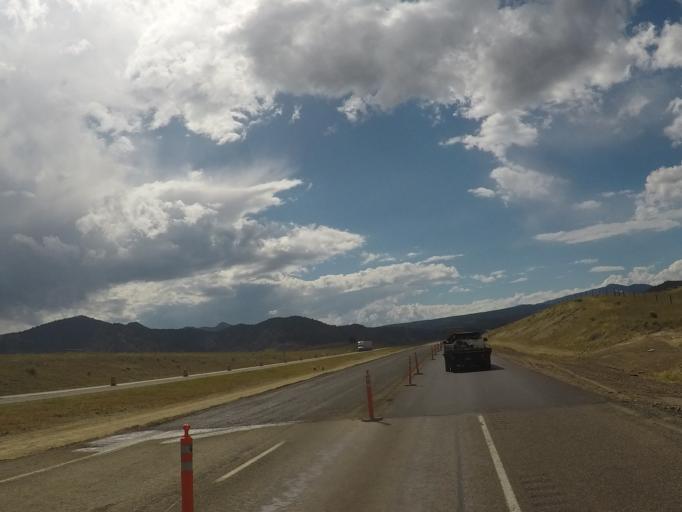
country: US
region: Montana
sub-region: Jefferson County
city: Whitehall
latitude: 45.9038
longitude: -112.2312
